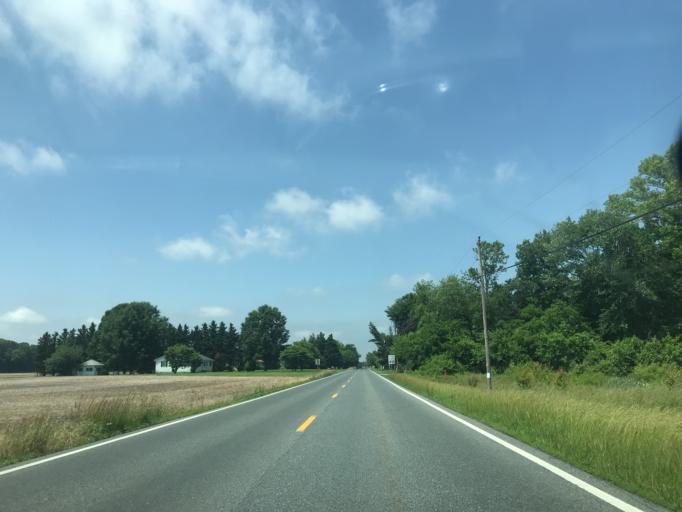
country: US
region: Maryland
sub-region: Dorchester County
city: Hurlock
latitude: 38.5978
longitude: -75.9528
